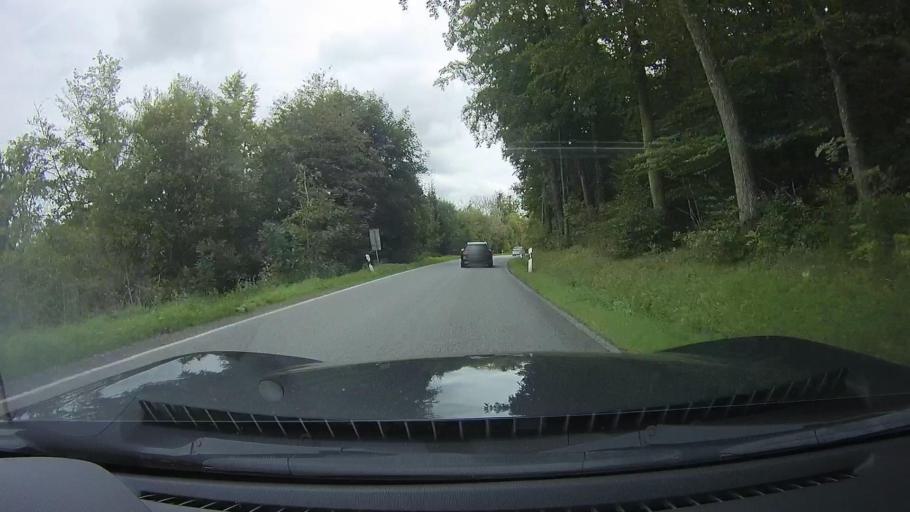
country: DE
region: Baden-Wuerttemberg
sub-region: Regierungsbezirk Stuttgart
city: Mainhardt
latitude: 49.0361
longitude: 9.5652
